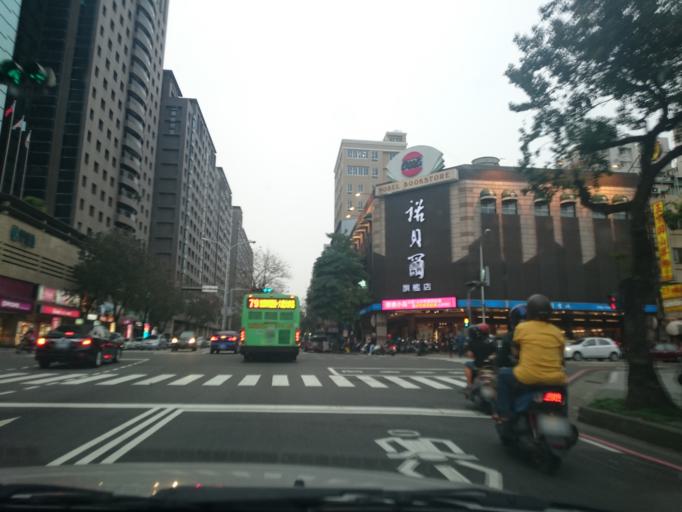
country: TW
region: Taiwan
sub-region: Taichung City
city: Taichung
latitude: 24.1506
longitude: 120.6574
